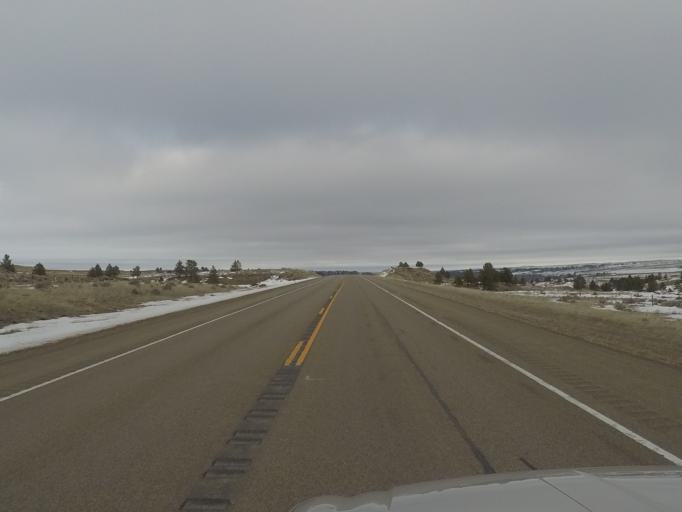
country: US
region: Montana
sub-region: Golden Valley County
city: Ryegate
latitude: 46.3189
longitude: -109.1594
